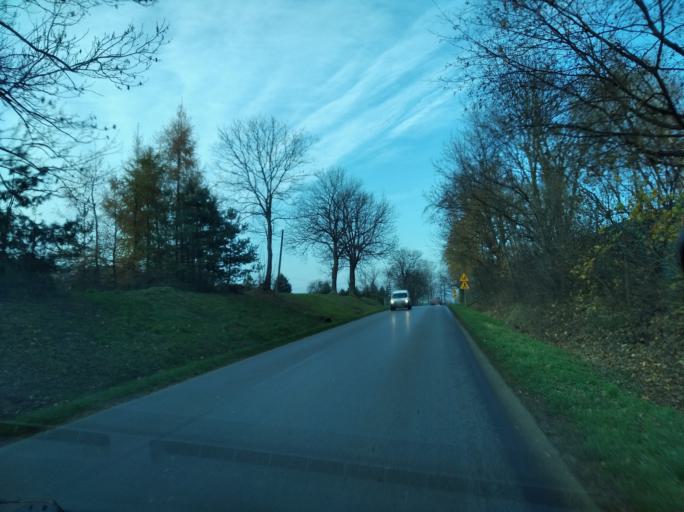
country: PL
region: Subcarpathian Voivodeship
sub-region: Powiat ropczycko-sedziszowski
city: Iwierzyce
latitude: 50.0472
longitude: 21.7449
